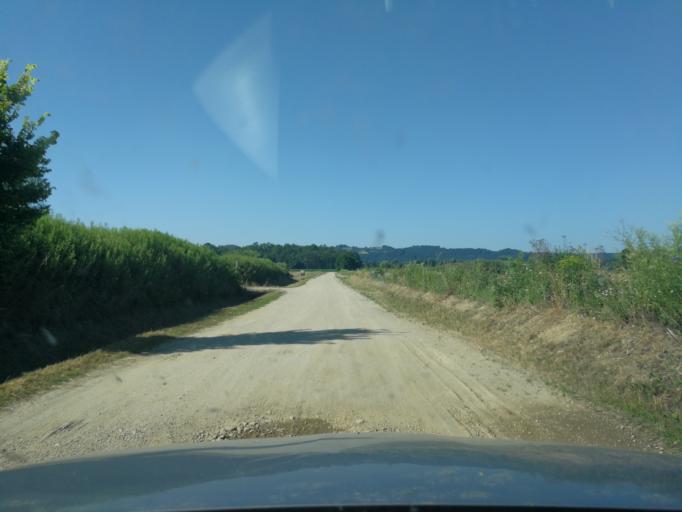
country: AT
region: Burgenland
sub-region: Politischer Bezirk Jennersdorf
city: Konigsdorf
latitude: 47.0128
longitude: 16.1600
